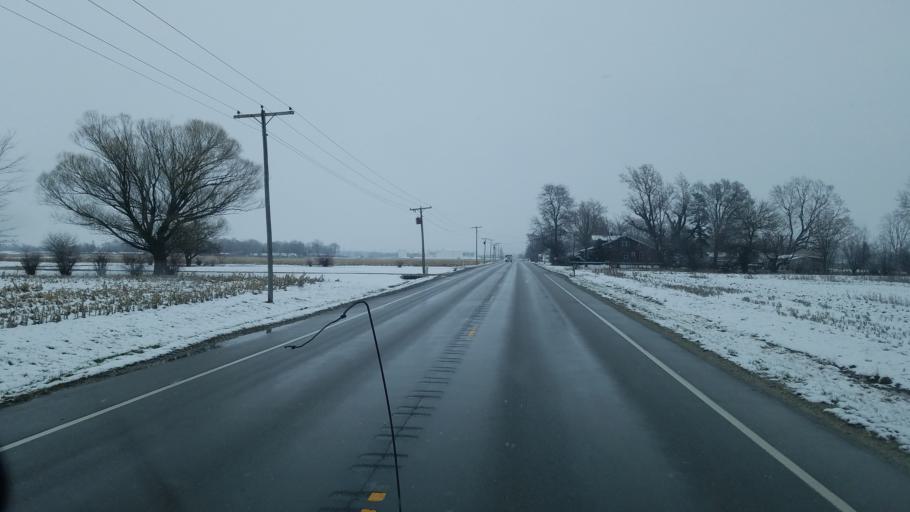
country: US
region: Indiana
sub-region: Delaware County
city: Eaton
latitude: 40.2770
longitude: -85.3786
